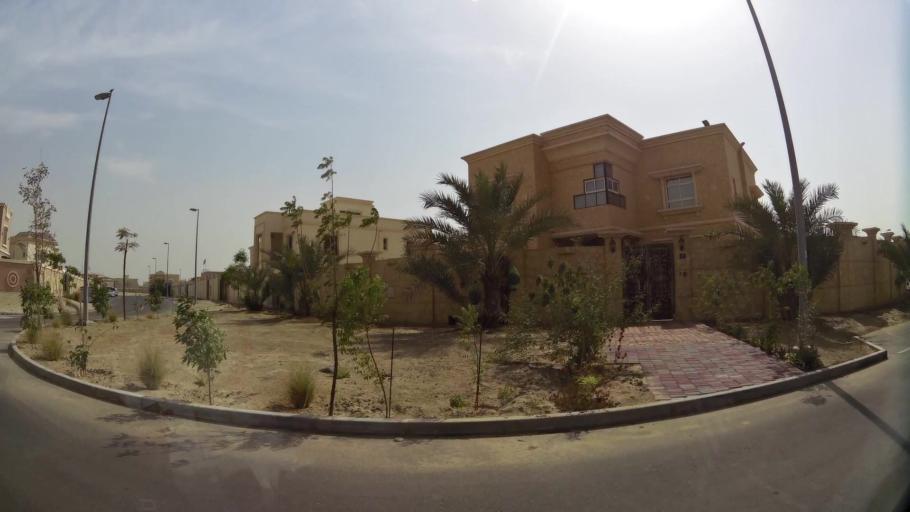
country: AE
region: Ash Shariqah
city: Sharjah
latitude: 25.2677
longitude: 55.4699
